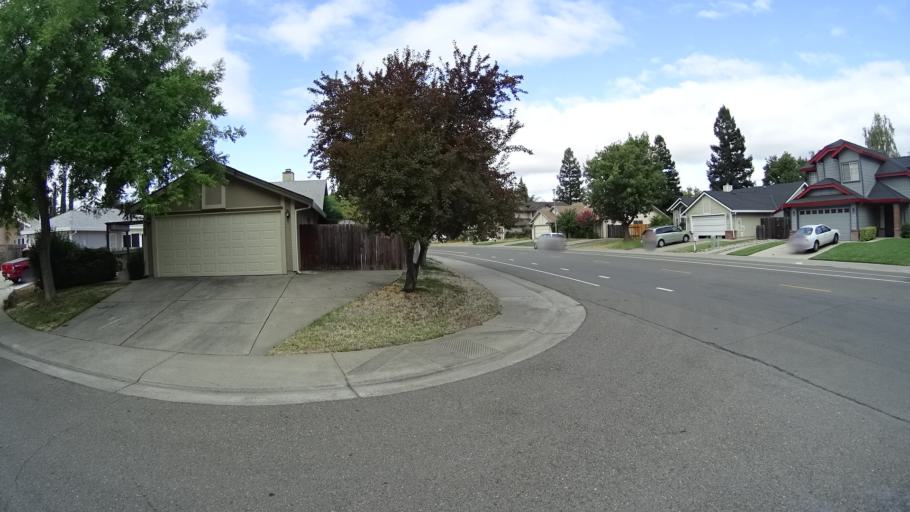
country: US
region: California
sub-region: Sacramento County
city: Laguna
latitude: 38.4199
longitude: -121.4221
